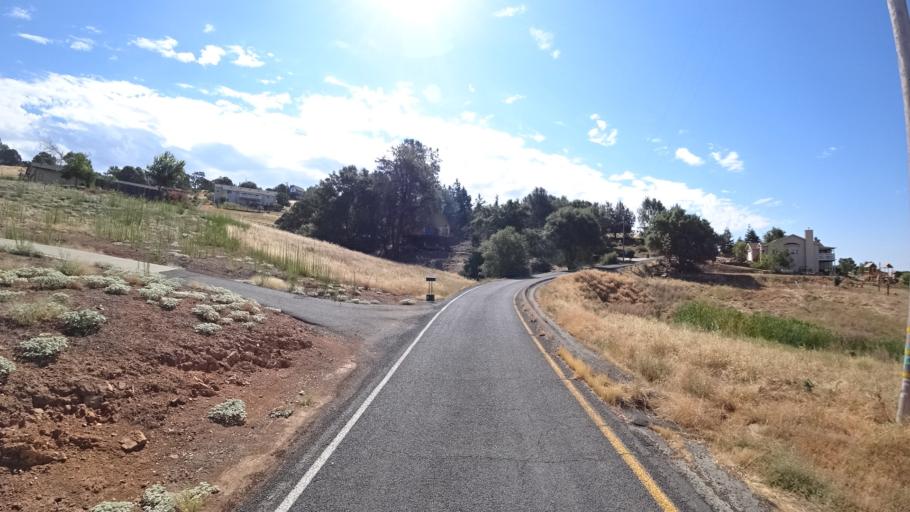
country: US
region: California
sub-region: Calaveras County
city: Copperopolis
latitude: 37.9290
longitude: -120.6367
